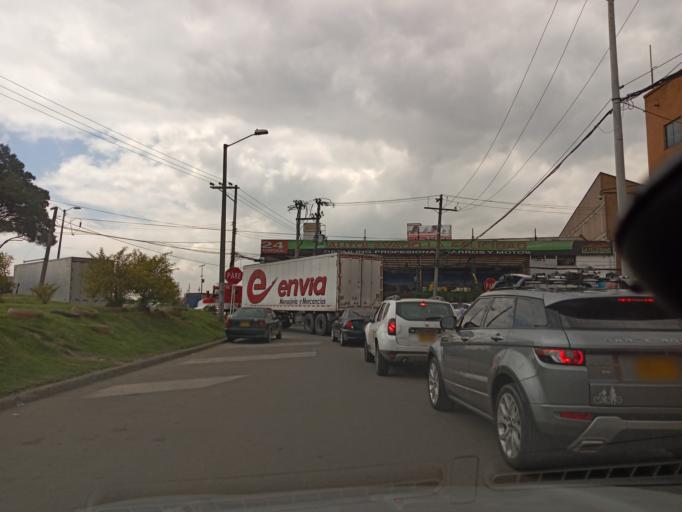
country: CO
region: Bogota D.C.
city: Bogota
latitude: 4.6467
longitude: -74.1243
